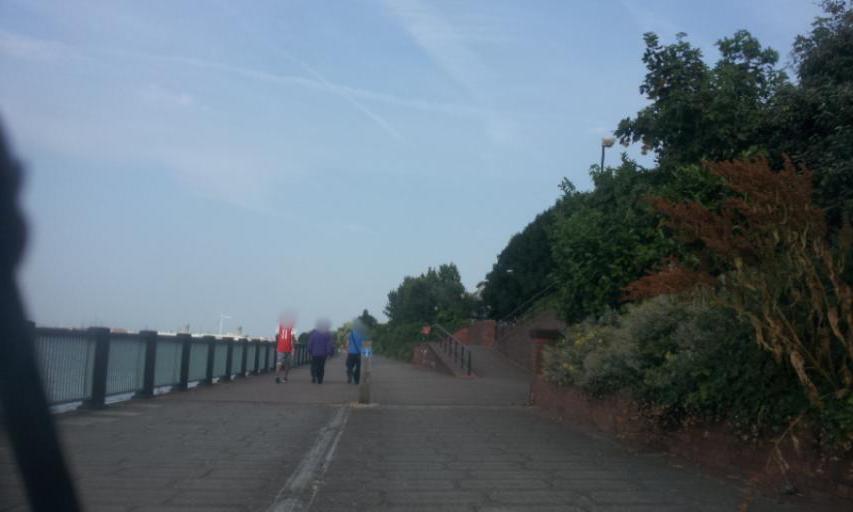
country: GB
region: England
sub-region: Greater London
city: Abbey Wood
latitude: 51.5106
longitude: 0.1166
